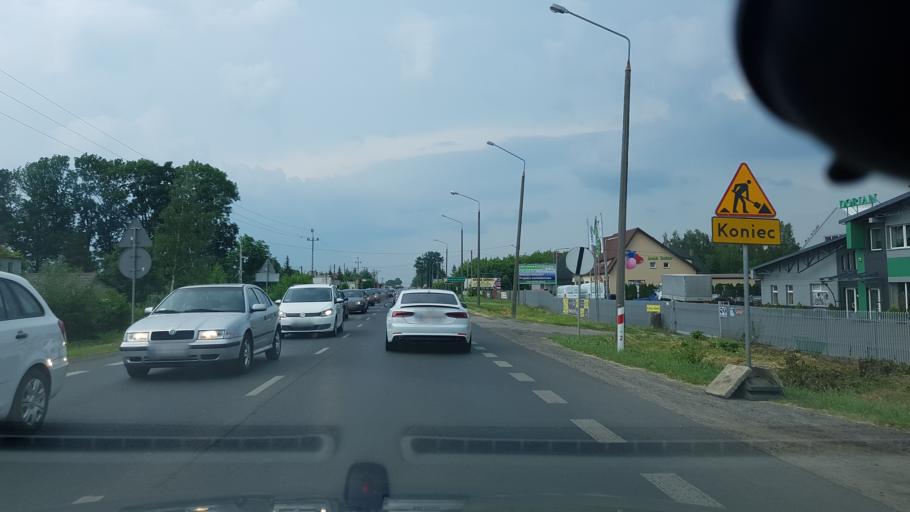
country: PL
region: Masovian Voivodeship
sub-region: Powiat legionowski
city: Michalow-Reginow
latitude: 52.4127
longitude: 20.9606
